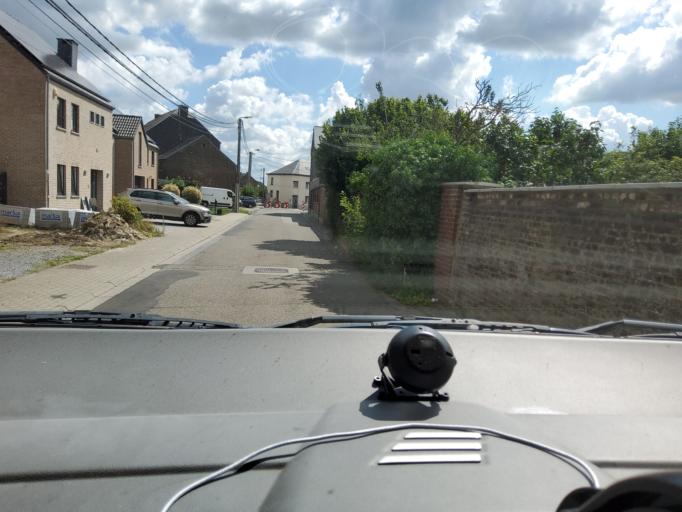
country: BE
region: Wallonia
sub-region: Province du Hainaut
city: Fleurus
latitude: 50.5144
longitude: 4.5662
